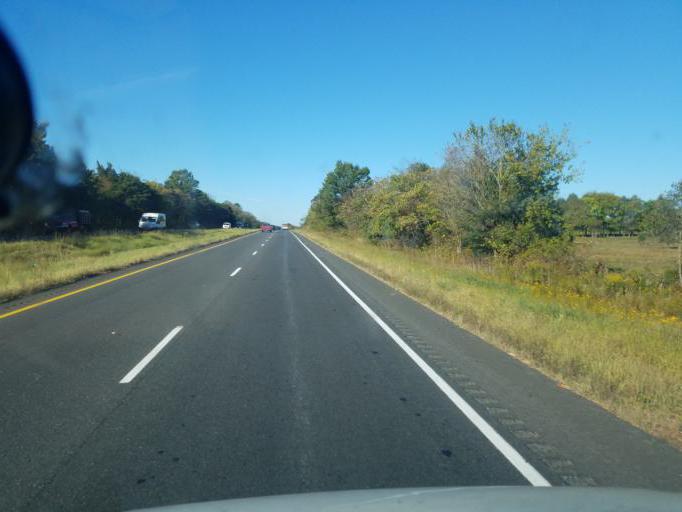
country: US
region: Virginia
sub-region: Fauquier County
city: Bealeton
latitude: 38.5099
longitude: -77.8653
